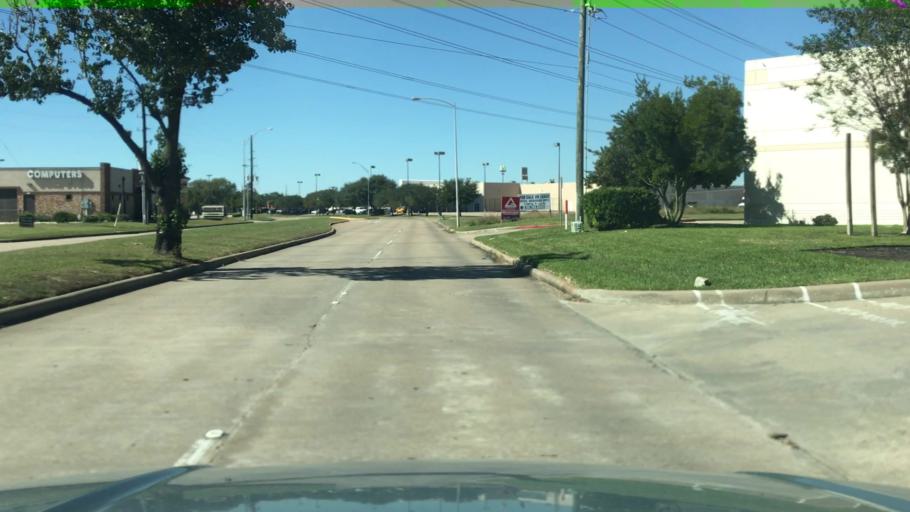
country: US
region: Texas
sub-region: Fort Bend County
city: Cinco Ranch
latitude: 29.7790
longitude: -95.7474
